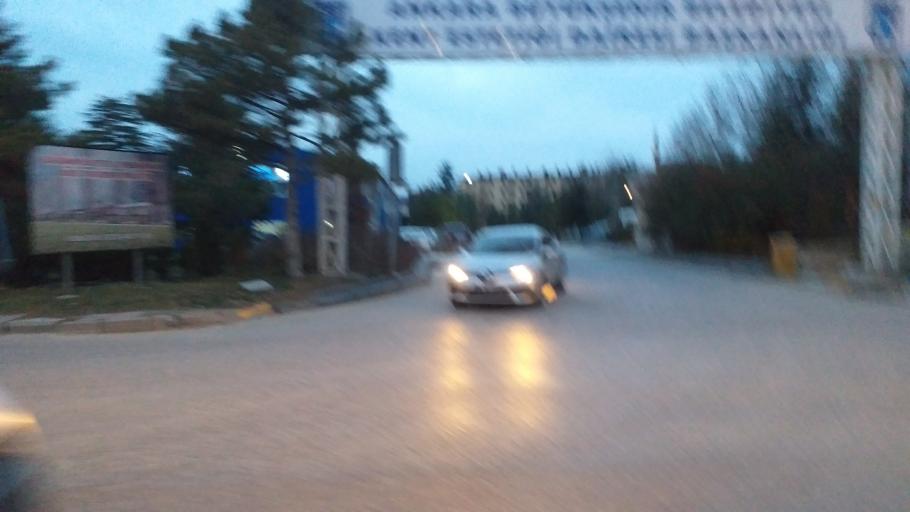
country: TR
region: Ankara
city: Ankara
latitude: 39.9652
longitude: 32.8203
